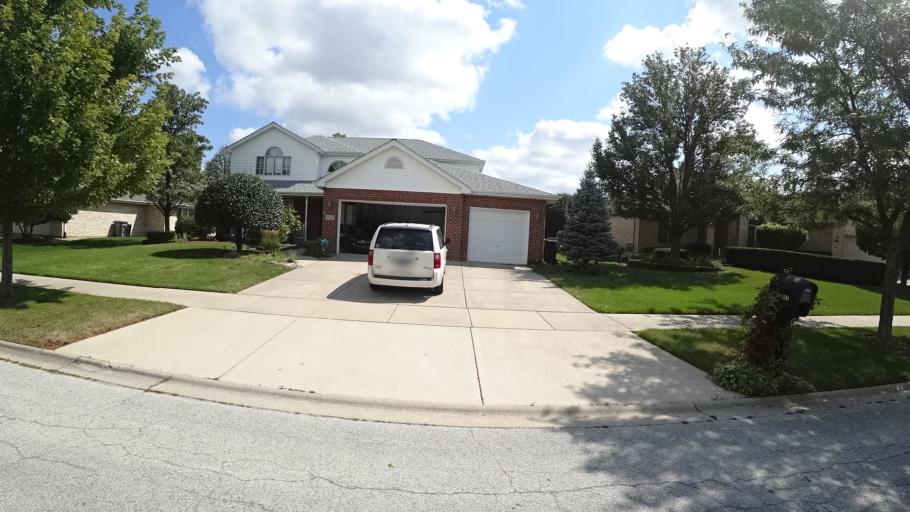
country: US
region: Illinois
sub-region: Will County
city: Mokena
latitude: 41.5703
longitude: -87.8852
